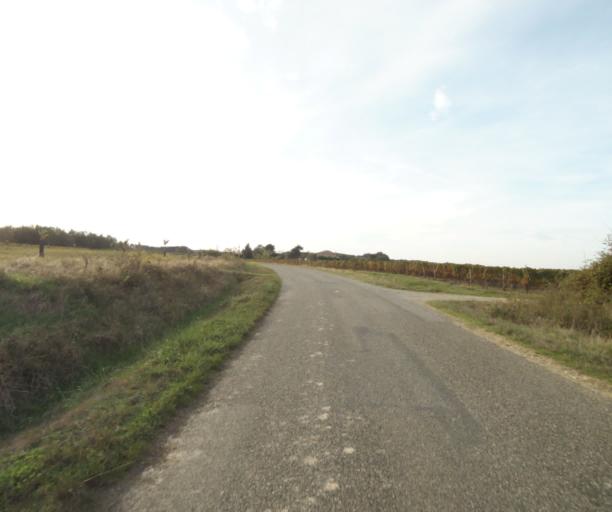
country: FR
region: Midi-Pyrenees
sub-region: Departement du Tarn-et-Garonne
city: Campsas
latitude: 43.8703
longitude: 1.3406
